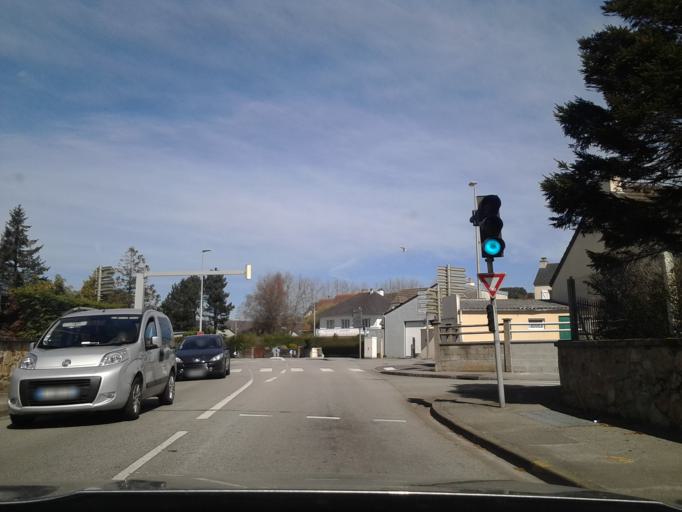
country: FR
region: Lower Normandy
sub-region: Departement de la Manche
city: Tourlaville
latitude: 49.6398
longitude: -1.5730
